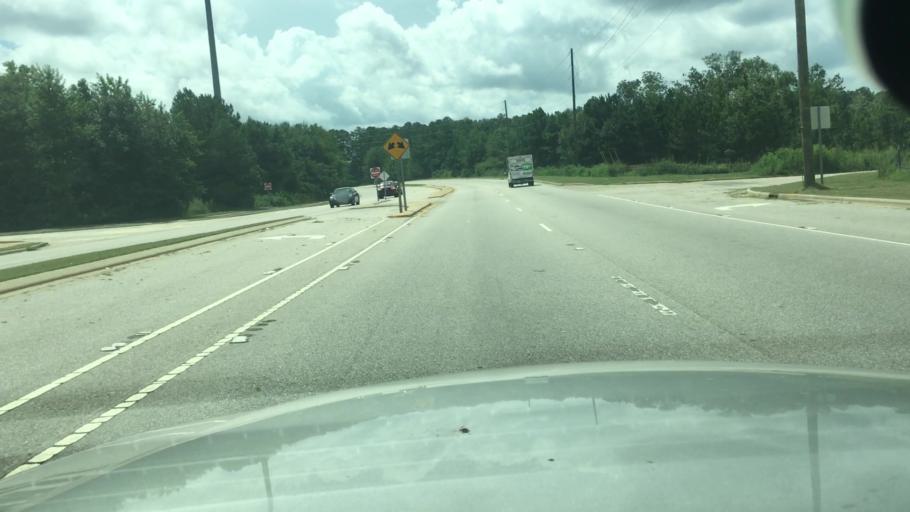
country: US
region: North Carolina
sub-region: Cumberland County
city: Hope Mills
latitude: 35.0406
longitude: -78.9898
